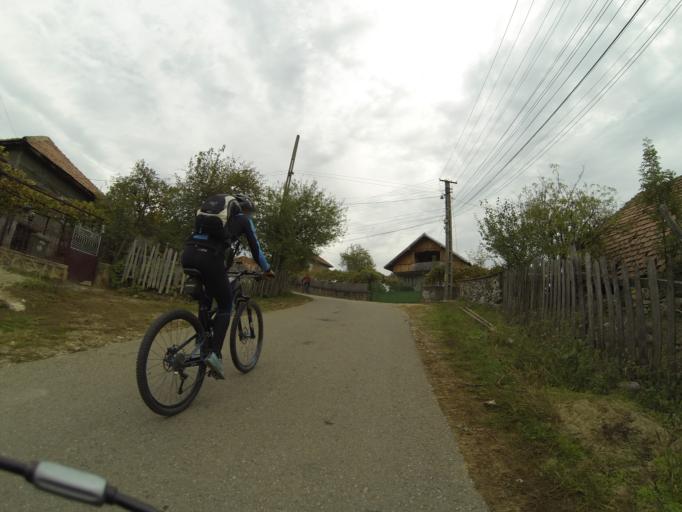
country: RO
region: Gorj
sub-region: Comuna Tismana
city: Sohodol
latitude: 45.0491
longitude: 22.8975
